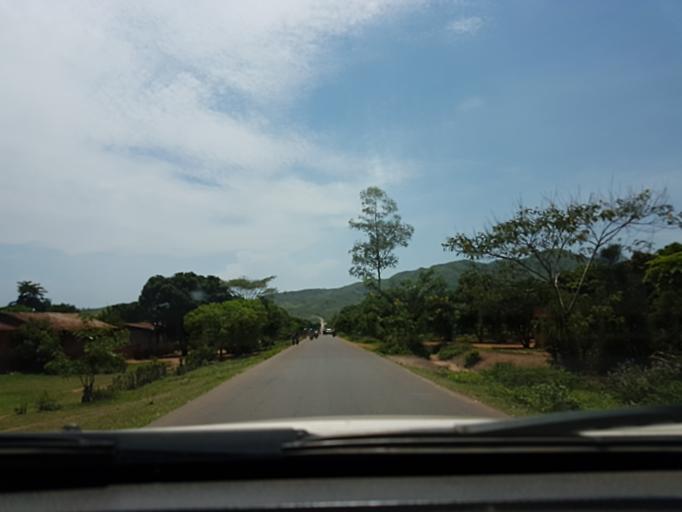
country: BI
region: Cibitoke
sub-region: Commune of Buganda
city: Buganda
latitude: -3.0823
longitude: 29.1253
